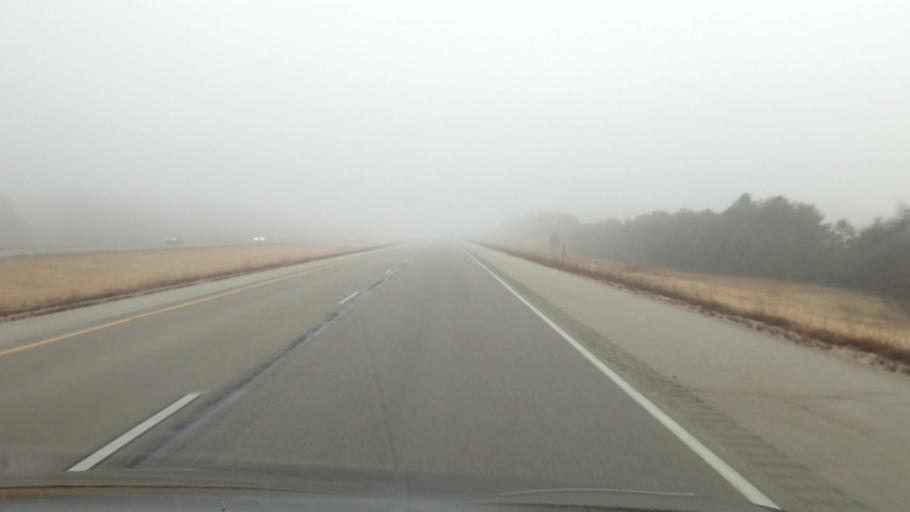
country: US
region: Wisconsin
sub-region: Walworth County
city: Elkhorn
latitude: 42.7086
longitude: -88.4815
